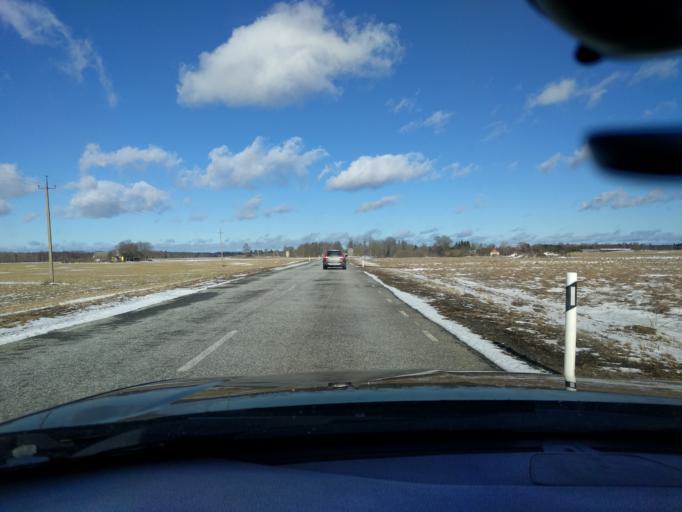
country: EE
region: Harju
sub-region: Raasiku vald
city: Raasiku
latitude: 59.3916
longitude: 25.1876
